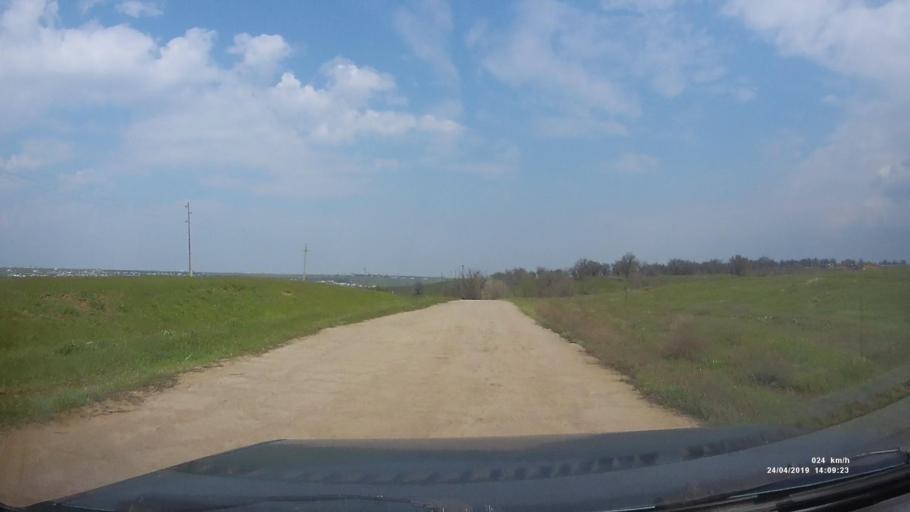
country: RU
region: Kalmykiya
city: Arshan'
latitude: 46.2637
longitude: 44.2222
